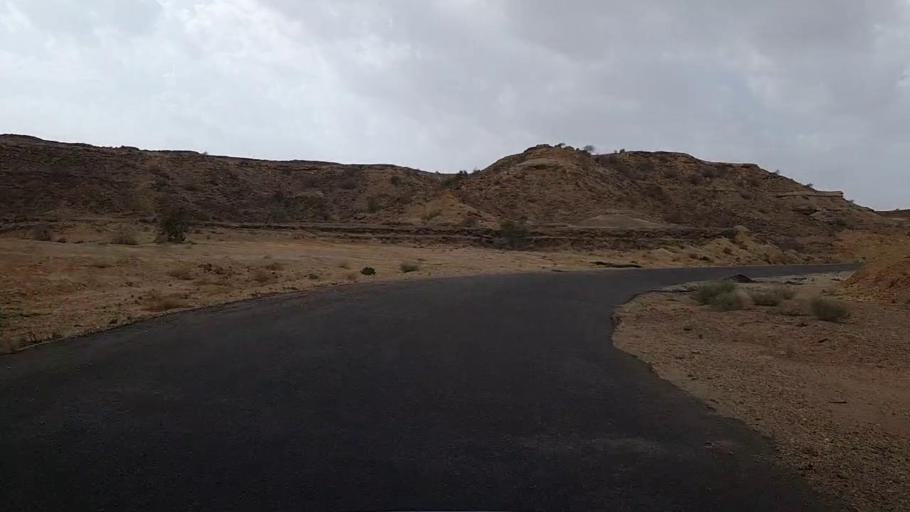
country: PK
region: Sindh
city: Jamshoro
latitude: 25.4227
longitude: 67.6909
